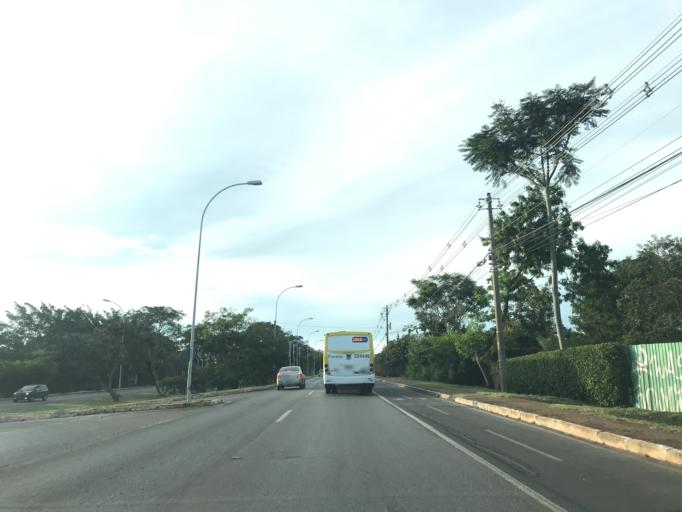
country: BR
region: Federal District
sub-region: Brasilia
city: Brasilia
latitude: -15.8192
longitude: -47.8054
